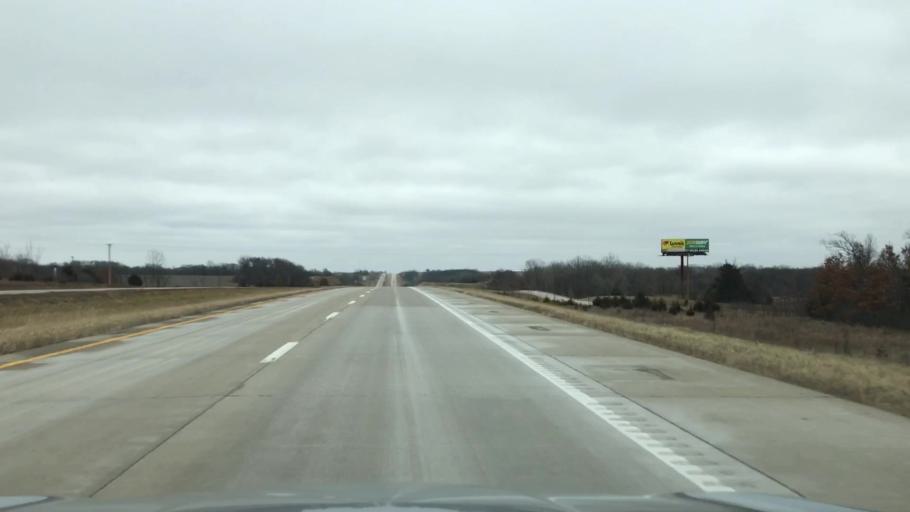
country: US
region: Missouri
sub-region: Livingston County
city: Chillicothe
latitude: 39.7356
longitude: -93.7432
